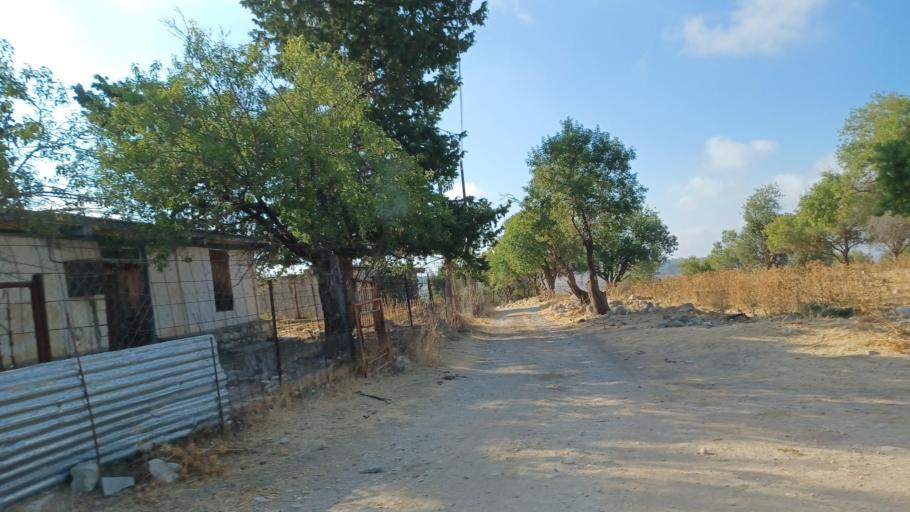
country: CY
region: Pafos
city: Mesogi
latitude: 34.8588
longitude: 32.5894
